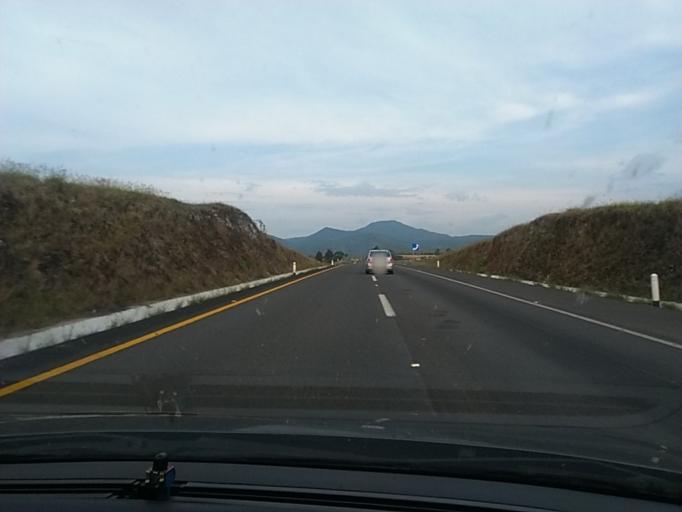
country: MX
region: Michoacan
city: Zinapecuaro
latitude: 19.9009
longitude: -100.8150
